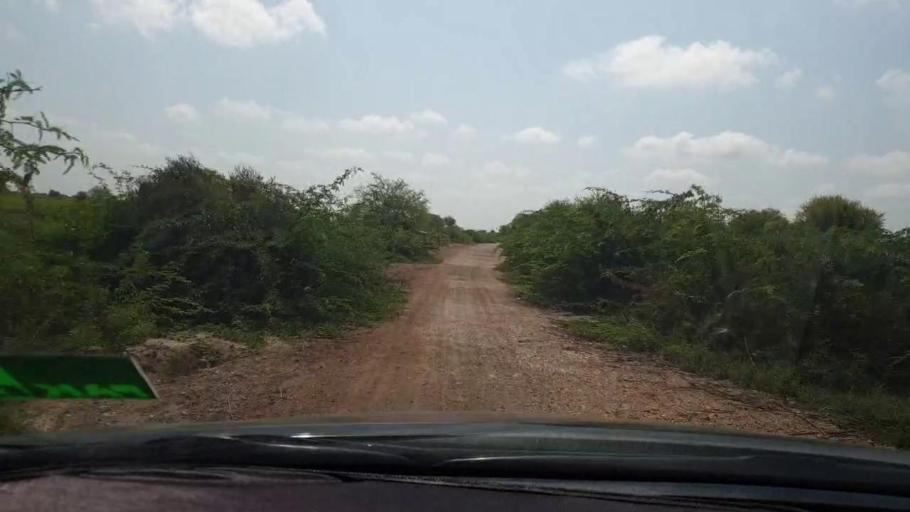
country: PK
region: Sindh
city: Tando Bago
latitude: 24.9377
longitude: 69.0937
